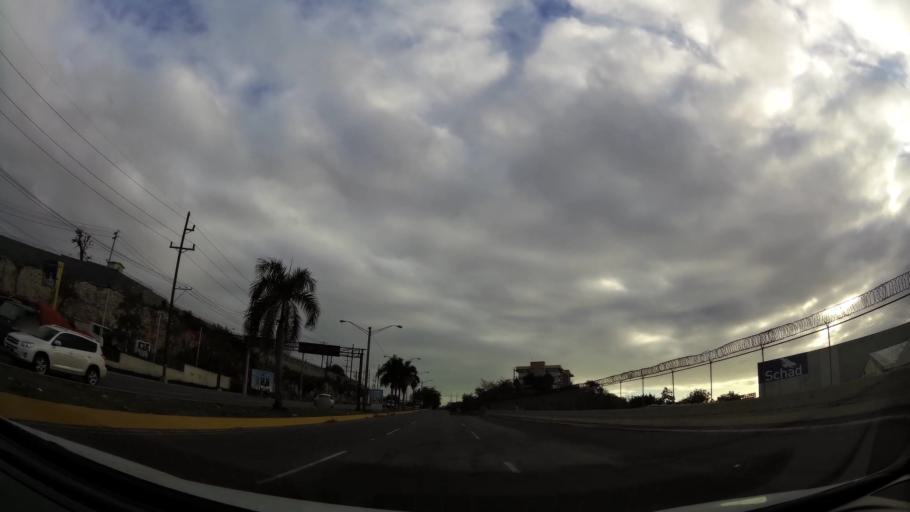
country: DO
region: San Cristobal
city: El Carril
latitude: 18.4305
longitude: -69.9885
